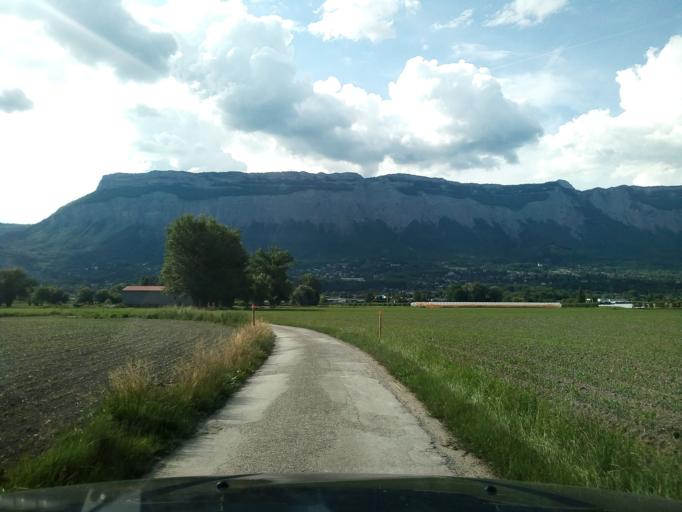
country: FR
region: Rhone-Alpes
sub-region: Departement de l'Isere
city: Domene
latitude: 45.2124
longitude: 5.8211
